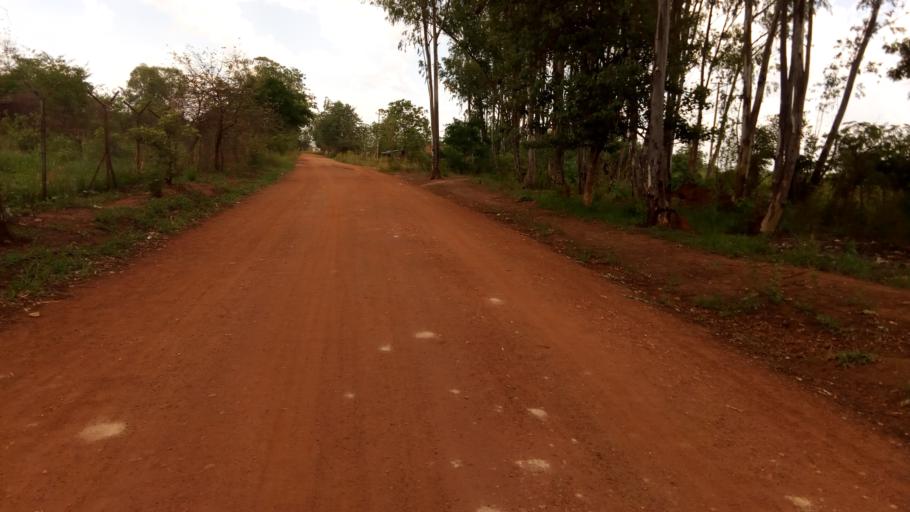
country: UG
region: Northern Region
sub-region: Gulu District
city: Gulu
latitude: 2.7883
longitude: 32.3489
